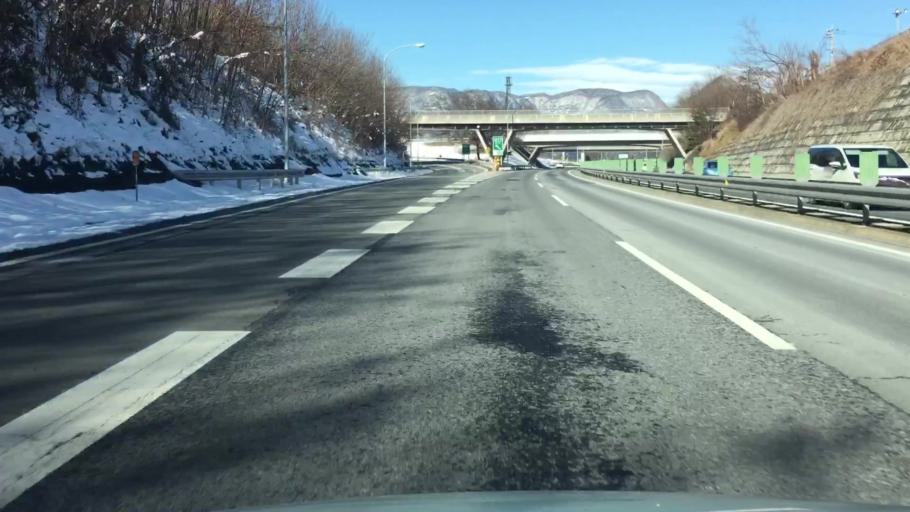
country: JP
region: Gunma
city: Numata
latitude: 36.6553
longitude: 139.0712
